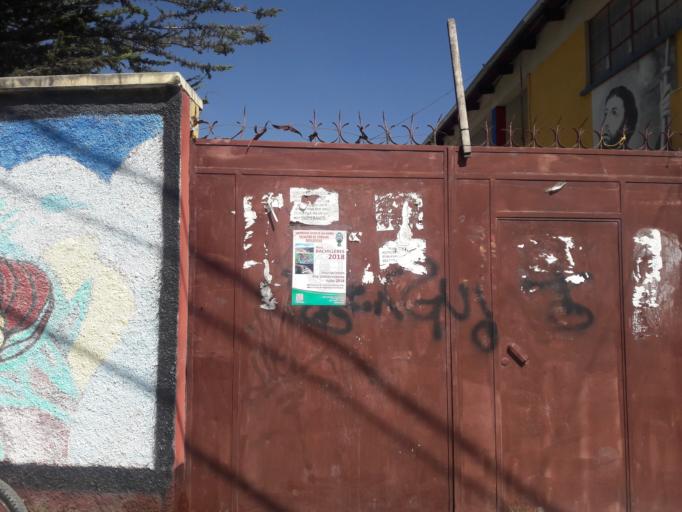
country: BO
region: La Paz
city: La Paz
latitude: -16.4868
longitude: -68.1510
